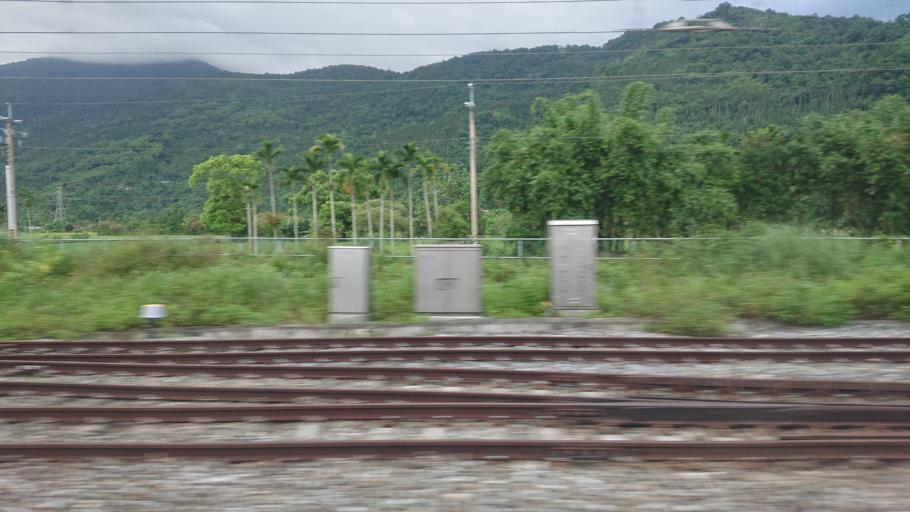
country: TW
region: Taiwan
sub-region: Hualien
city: Hualian
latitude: 23.6666
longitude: 121.4210
